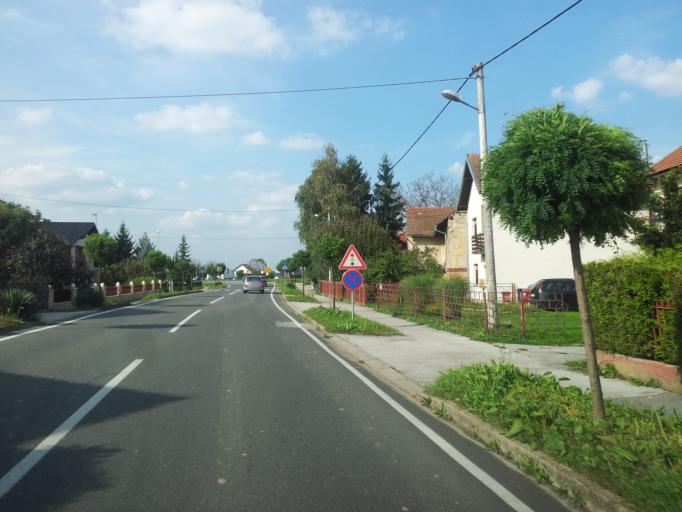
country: HR
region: Varazdinska
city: Jalkovec
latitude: 46.2603
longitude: 16.3630
